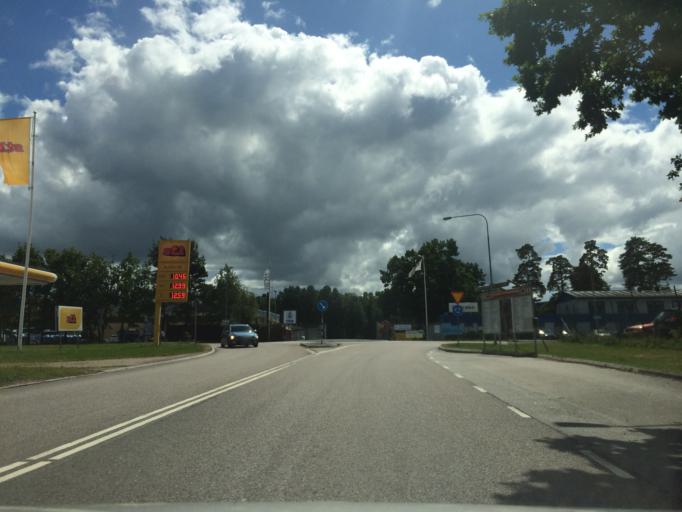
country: SE
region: Vaestra Goetaland
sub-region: Trollhattan
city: Trollhattan
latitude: 58.2947
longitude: 12.3216
